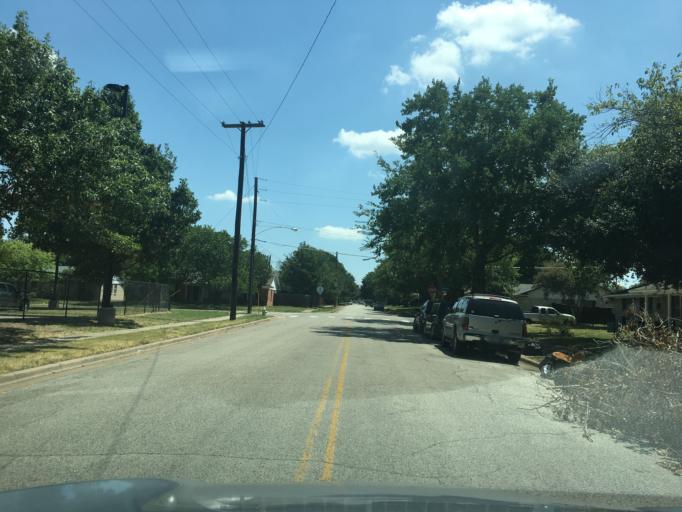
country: US
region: Texas
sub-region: Dallas County
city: Garland
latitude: 32.8695
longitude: -96.6876
